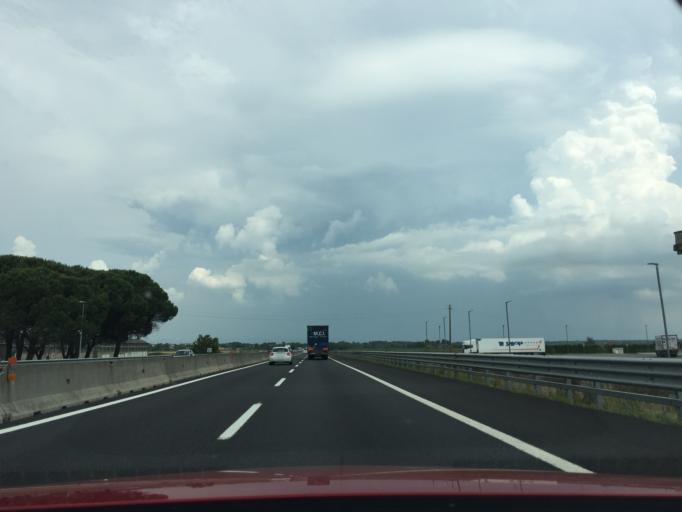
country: IT
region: Tuscany
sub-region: Provincia di Lucca
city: Porcari
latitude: 43.8192
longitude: 10.6262
